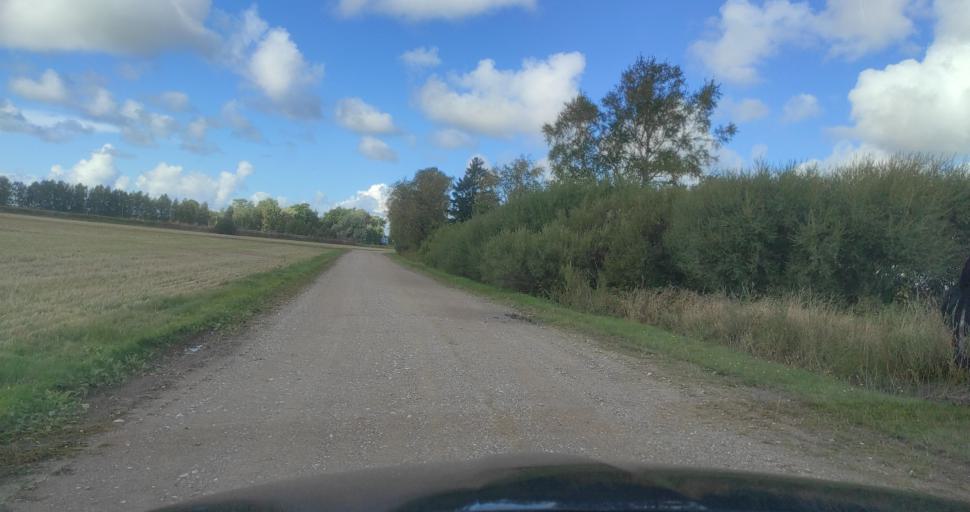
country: LV
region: Ventspils Rajons
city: Piltene
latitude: 57.2708
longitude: 21.5873
